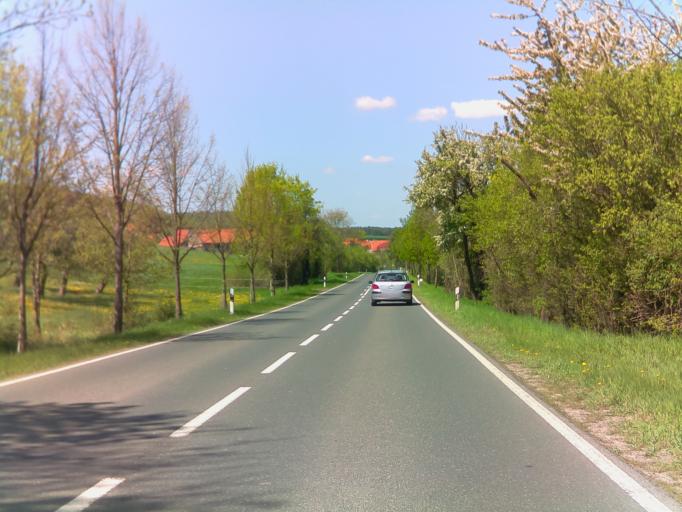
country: DE
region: Thuringia
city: Behringen
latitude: 50.7921
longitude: 10.9858
